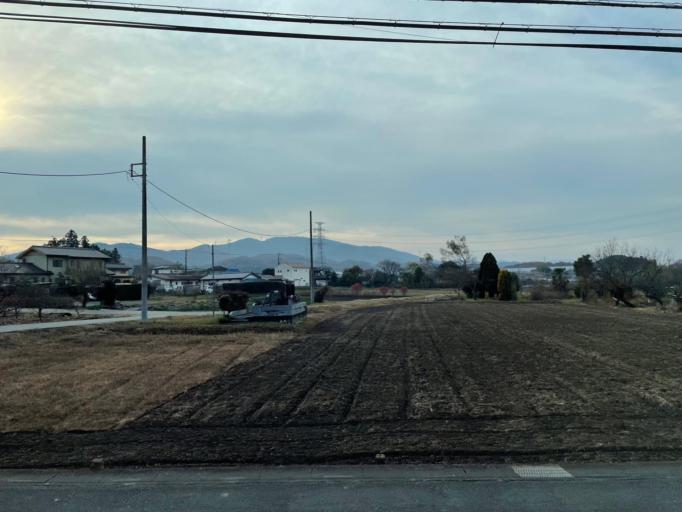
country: JP
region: Saitama
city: Yorii
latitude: 36.1591
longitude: 139.1862
